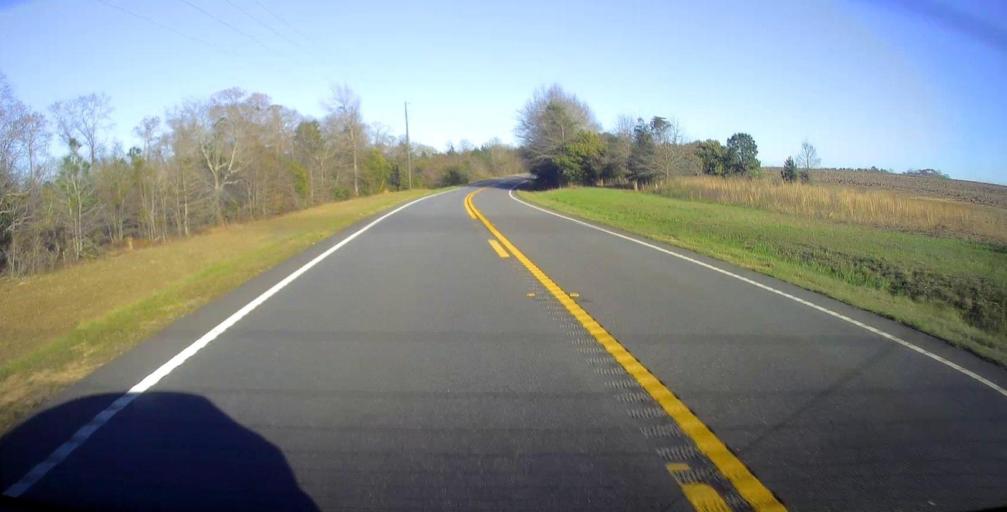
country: US
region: Georgia
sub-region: Taylor County
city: Butler
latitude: 32.5008
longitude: -84.4090
